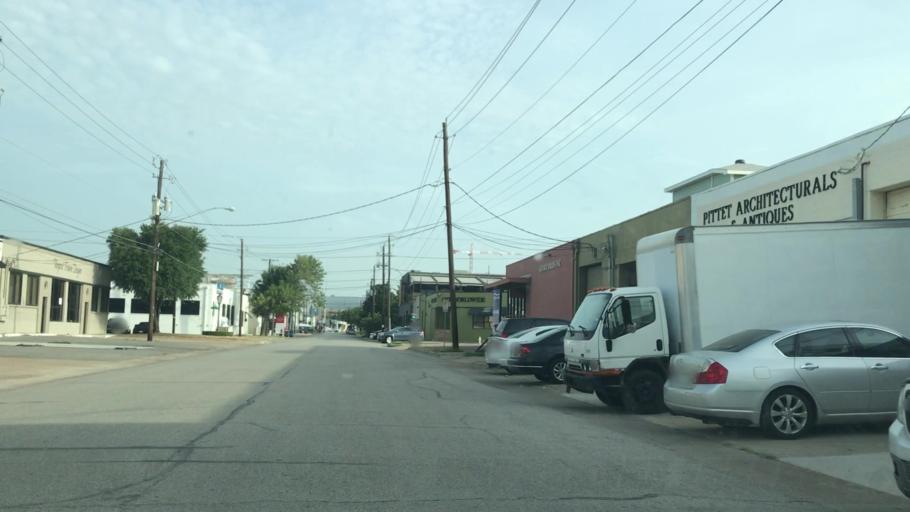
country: US
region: Texas
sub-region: Dallas County
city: Dallas
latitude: 32.7898
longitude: -96.8185
